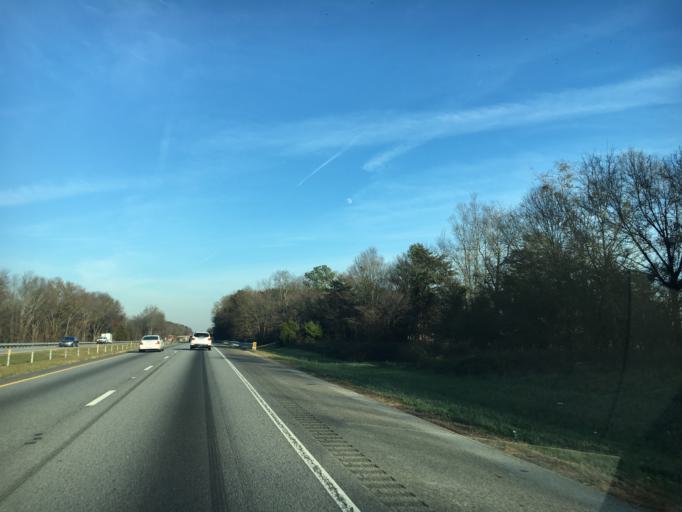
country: US
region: South Carolina
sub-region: Anderson County
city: Centerville
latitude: 34.5544
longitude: -82.7846
